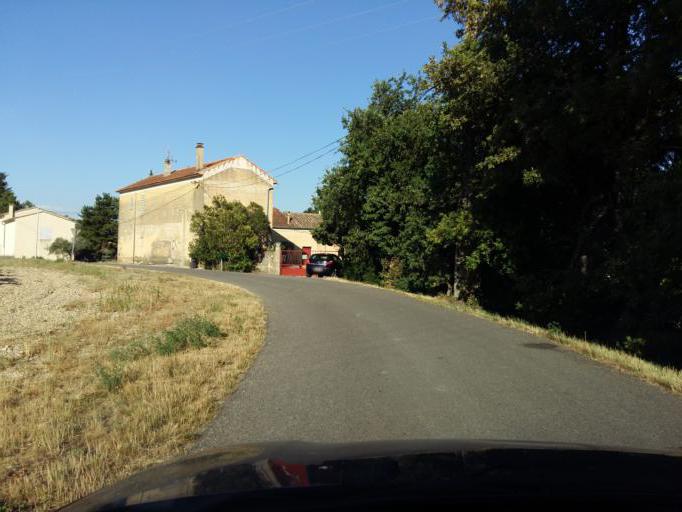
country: FR
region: Provence-Alpes-Cote d'Azur
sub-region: Departement du Vaucluse
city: Camaret-sur-Aigues
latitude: 44.1667
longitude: 4.8887
